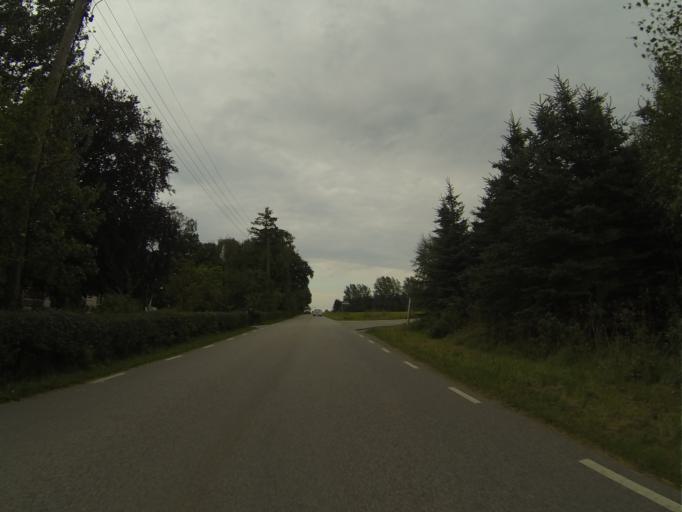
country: SE
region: Skane
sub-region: Staffanstorps Kommun
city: Hjaerup
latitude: 55.6253
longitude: 13.1266
